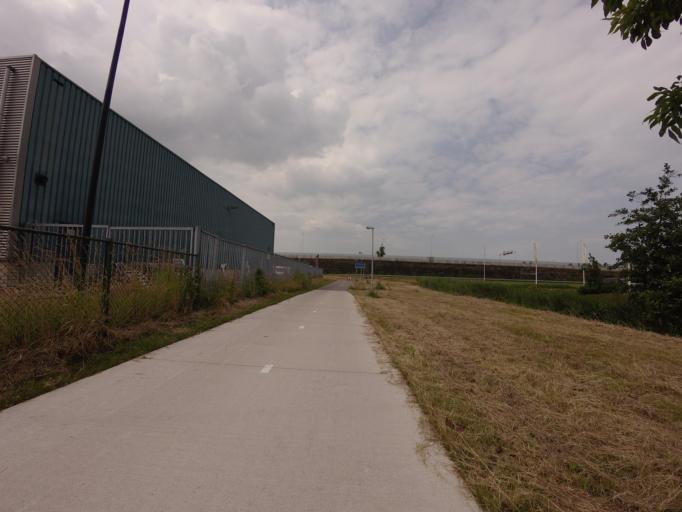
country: NL
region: North Holland
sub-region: Gemeente Hoorn
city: Hoorn
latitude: 52.6717
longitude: 5.0609
